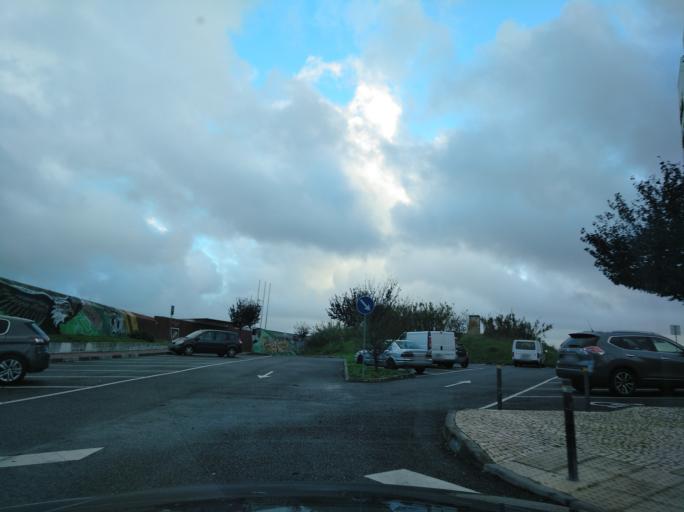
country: PT
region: Lisbon
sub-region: Lisbon
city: Lisbon
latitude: 38.7436
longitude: -9.1109
